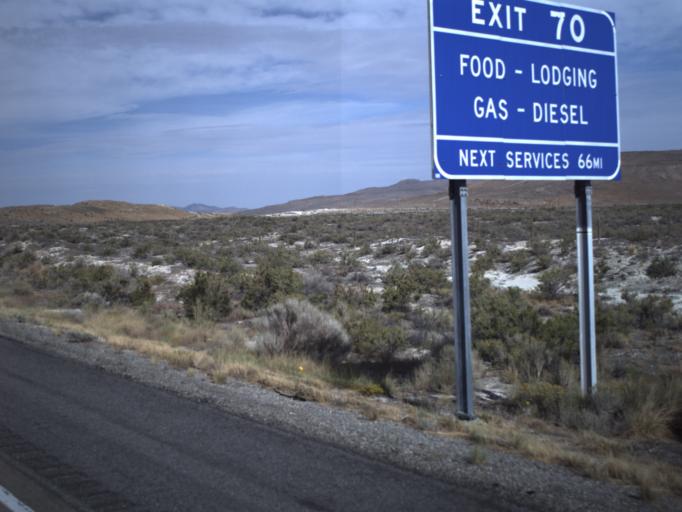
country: US
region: Utah
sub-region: Tooele County
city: Grantsville
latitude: 40.7577
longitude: -112.7680
